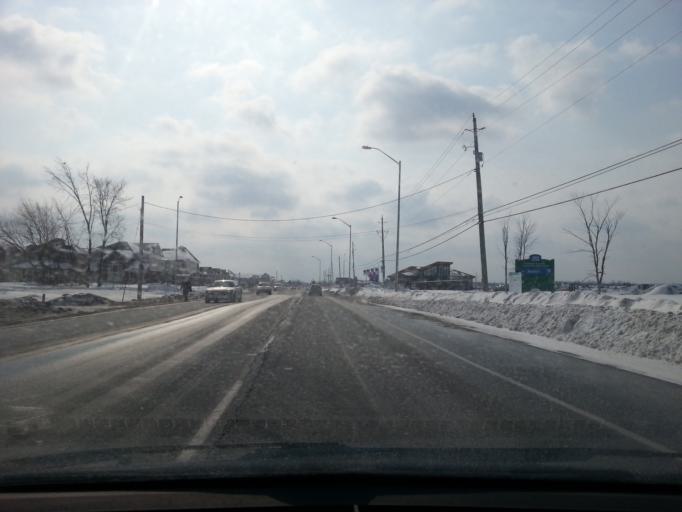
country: CA
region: Ontario
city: Clarence-Rockland
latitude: 45.4487
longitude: -75.4808
